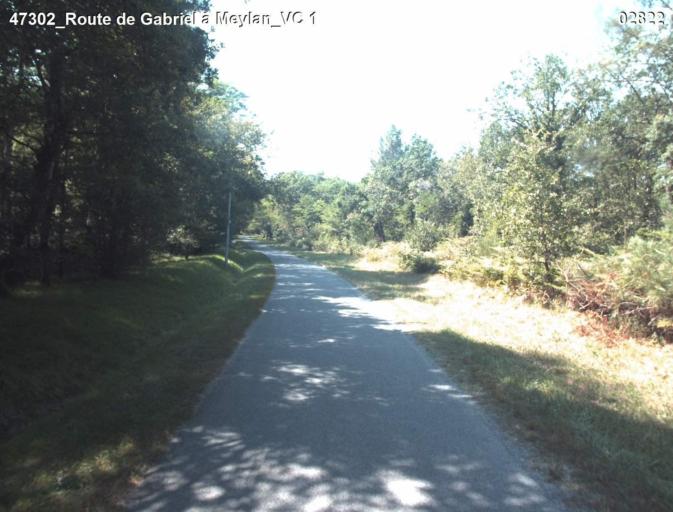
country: FR
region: Aquitaine
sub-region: Departement du Lot-et-Garonne
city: Mezin
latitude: 44.0721
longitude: 0.1294
